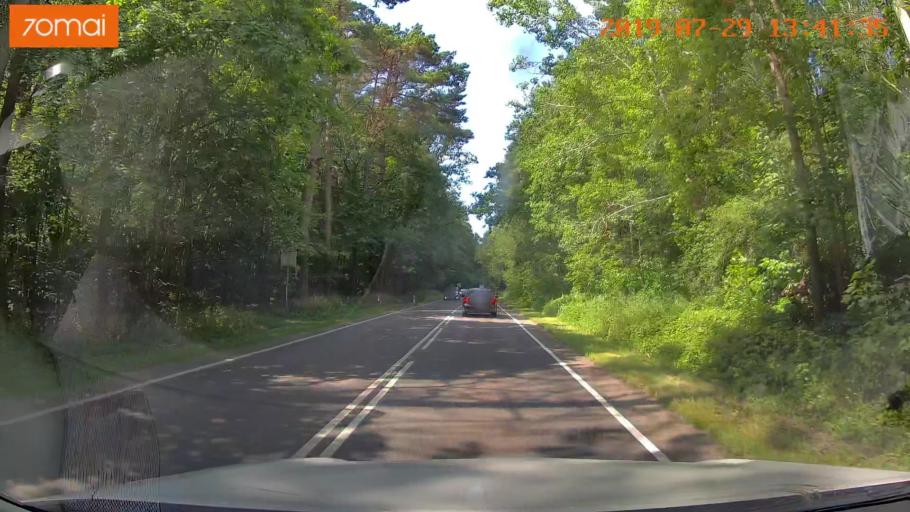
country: RU
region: Kaliningrad
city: Svetlyy
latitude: 54.7356
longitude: 20.1244
